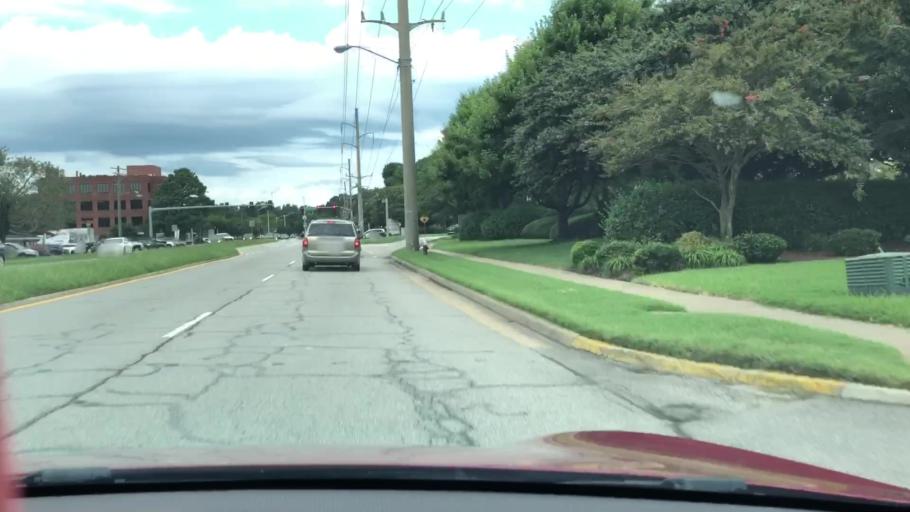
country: US
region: Virginia
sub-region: City of Virginia Beach
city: Virginia Beach
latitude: 36.8645
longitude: -76.0285
